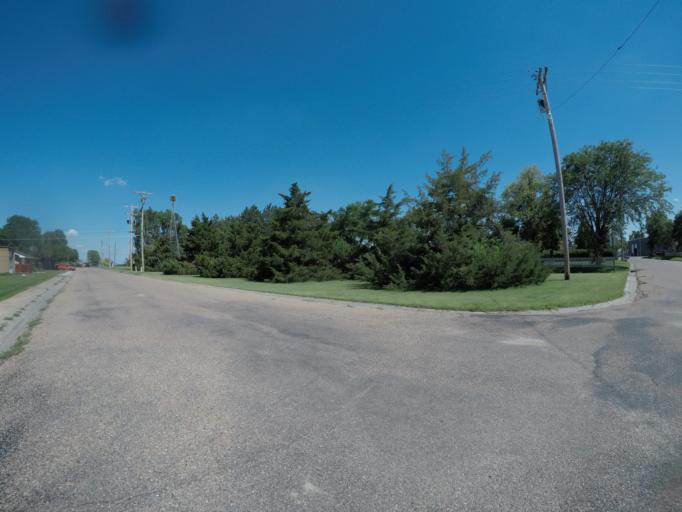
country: US
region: Kansas
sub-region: Sheridan County
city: Hoxie
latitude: 39.3589
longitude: -100.4370
